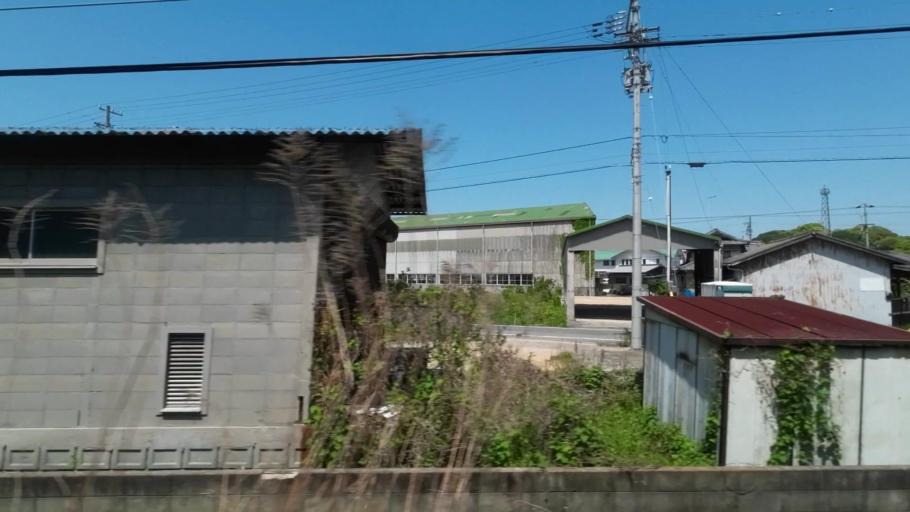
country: JP
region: Ehime
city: Hojo
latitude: 34.0382
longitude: 132.8467
